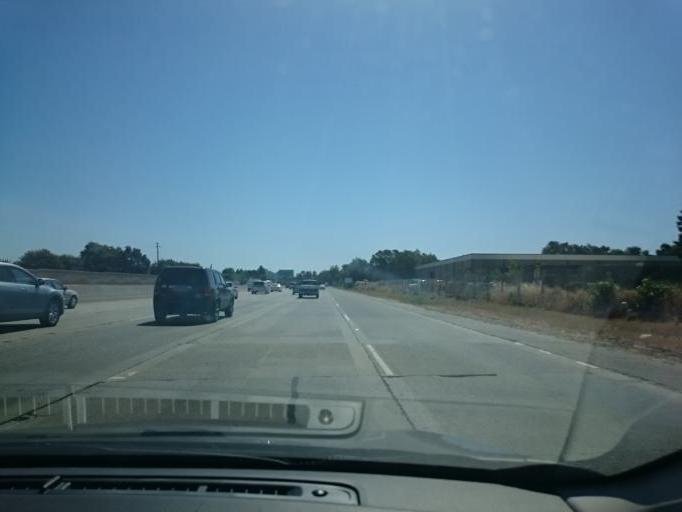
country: US
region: California
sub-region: Yolo County
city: West Sacramento
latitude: 38.5748
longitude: -121.5421
